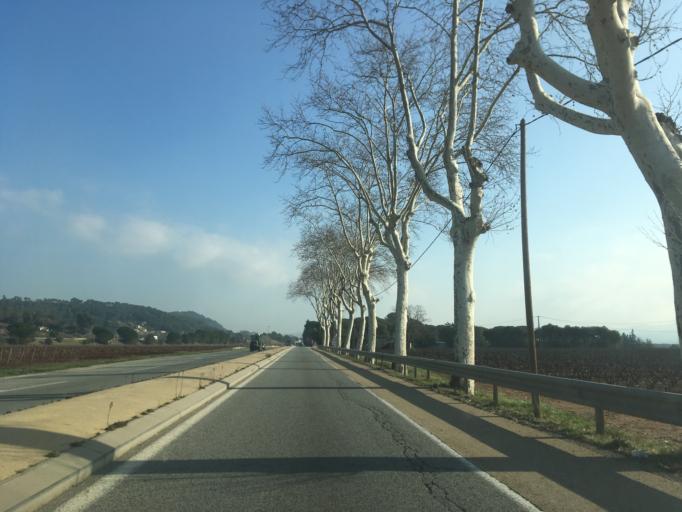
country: FR
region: Provence-Alpes-Cote d'Azur
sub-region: Departement du Var
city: Le Cannet-des-Maures
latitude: 43.3994
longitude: 6.3691
